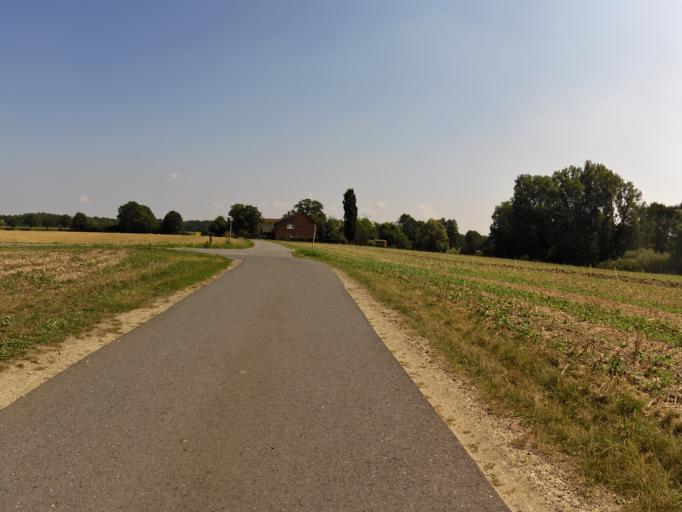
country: DE
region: North Rhine-Westphalia
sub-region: Regierungsbezirk Munster
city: Telgte
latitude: 51.9625
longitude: 7.7184
